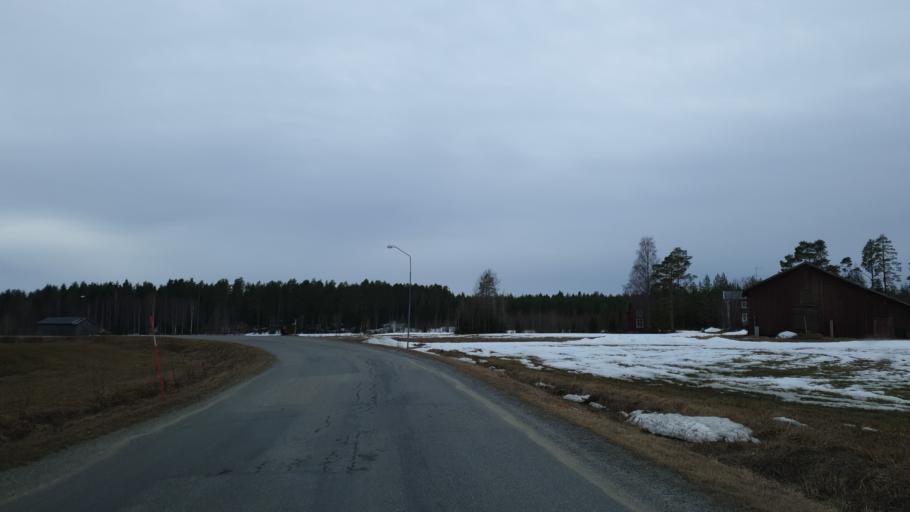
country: SE
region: Vaesterbotten
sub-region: Robertsfors Kommun
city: Robertsfors
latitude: 64.4003
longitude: 21.0044
